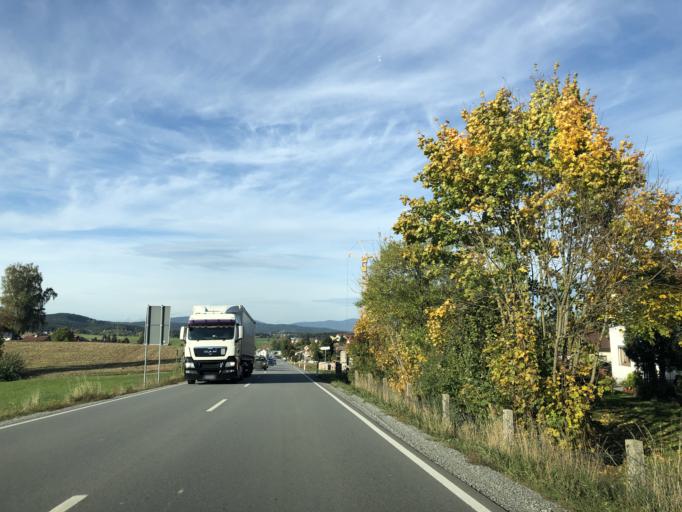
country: DE
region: Bavaria
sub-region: Lower Bavaria
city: Ruhmannsfelden
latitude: 48.9793
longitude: 12.9809
